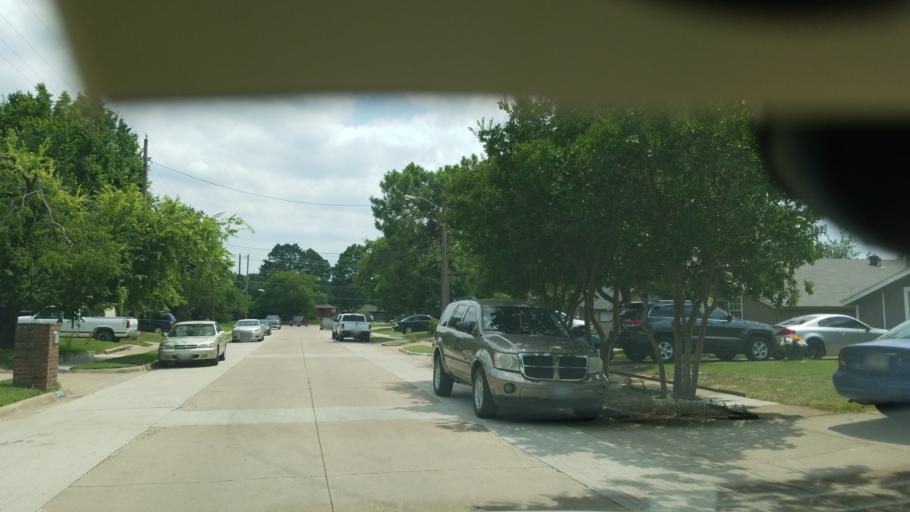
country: US
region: Texas
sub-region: Dallas County
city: Irving
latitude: 32.8467
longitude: -96.9569
